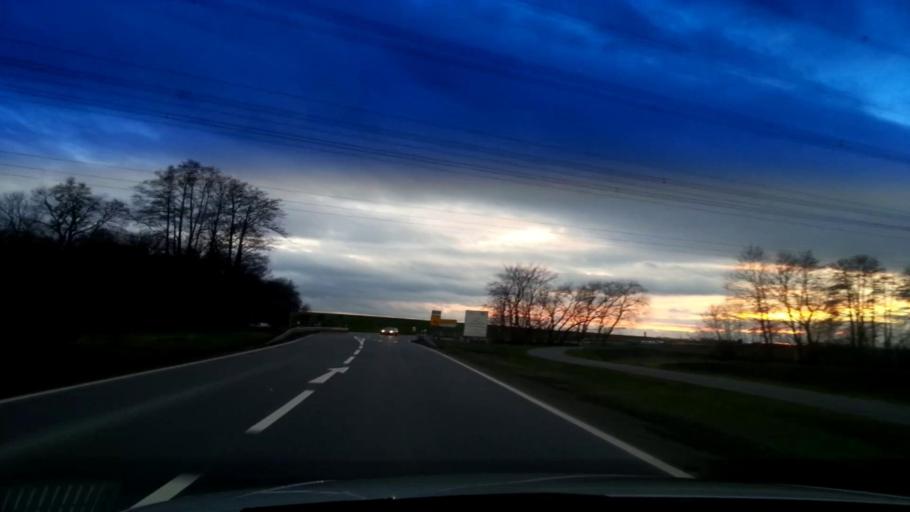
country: DE
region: Bavaria
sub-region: Upper Franconia
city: Schesslitz
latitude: 49.9671
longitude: 11.0221
